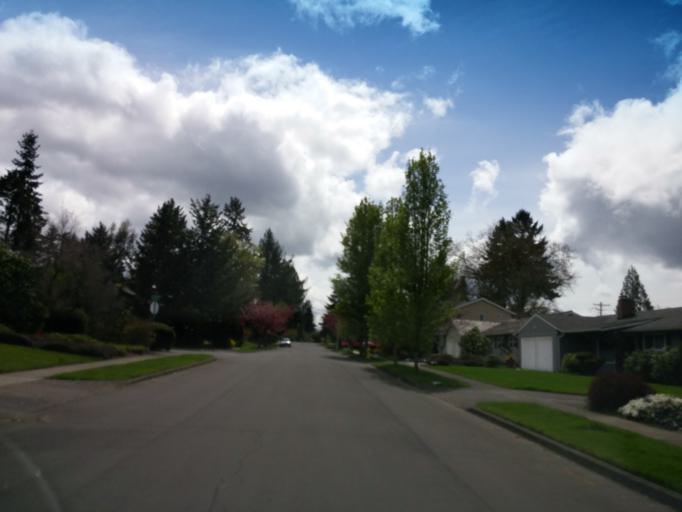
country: US
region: Oregon
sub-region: Washington County
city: Cedar Hills
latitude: 45.5069
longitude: -122.8100
